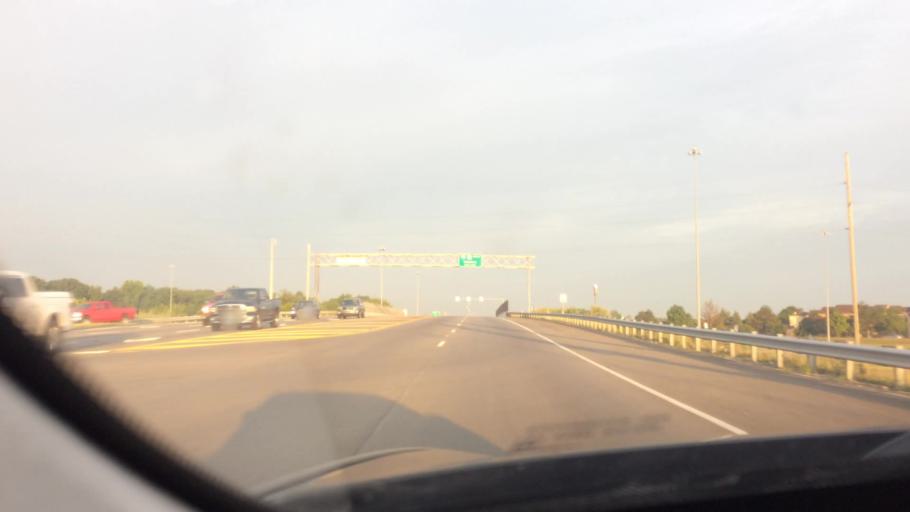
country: US
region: Ohio
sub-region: Lucas County
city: Holland
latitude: 41.6133
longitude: -83.6891
